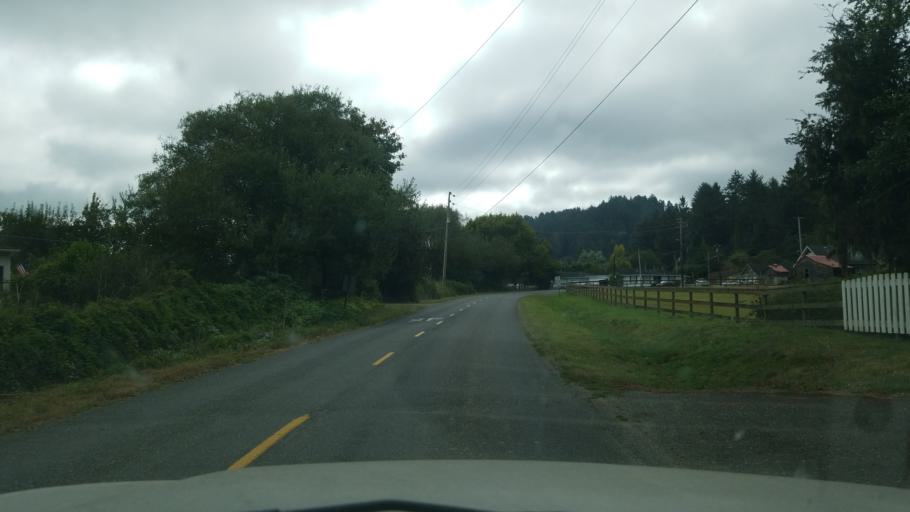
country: US
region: California
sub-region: Humboldt County
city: Ferndale
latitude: 40.5790
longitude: -124.2705
